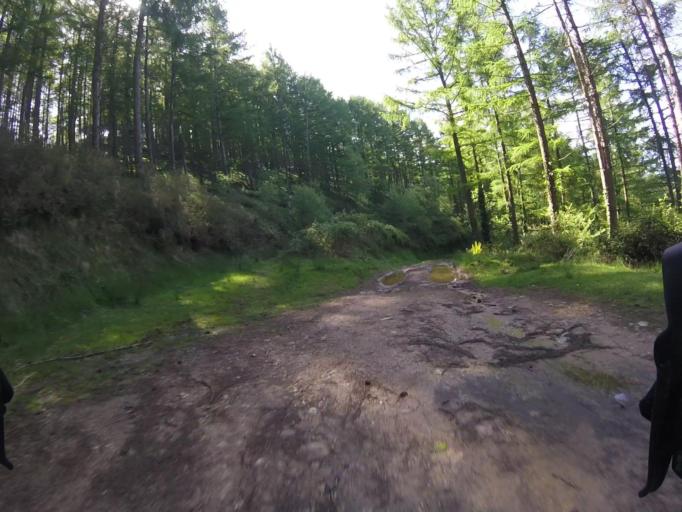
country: ES
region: Basque Country
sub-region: Provincia de Guipuzcoa
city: Urnieta
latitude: 43.1908
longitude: -1.9622
